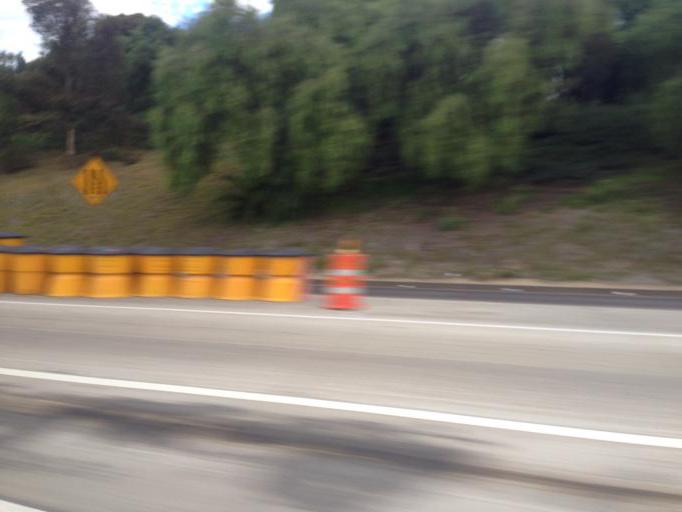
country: US
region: California
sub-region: San Diego County
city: National City
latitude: 32.6654
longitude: -117.0795
